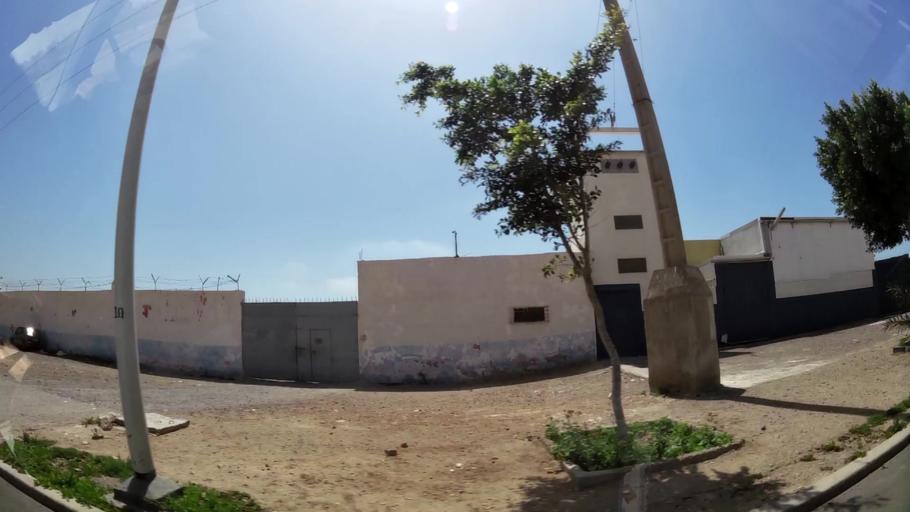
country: MA
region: Souss-Massa-Draa
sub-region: Agadir-Ida-ou-Tnan
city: Aourir
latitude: 30.4441
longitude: -9.6495
